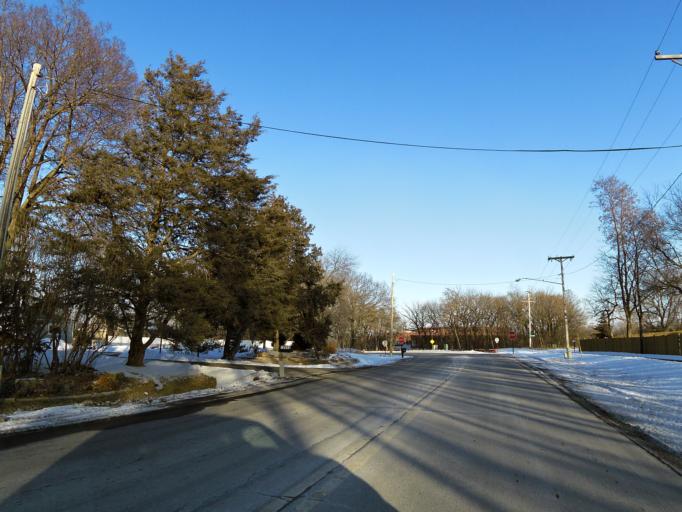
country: US
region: Minnesota
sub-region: Dakota County
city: Lakeville
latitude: 44.6537
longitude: -93.2693
